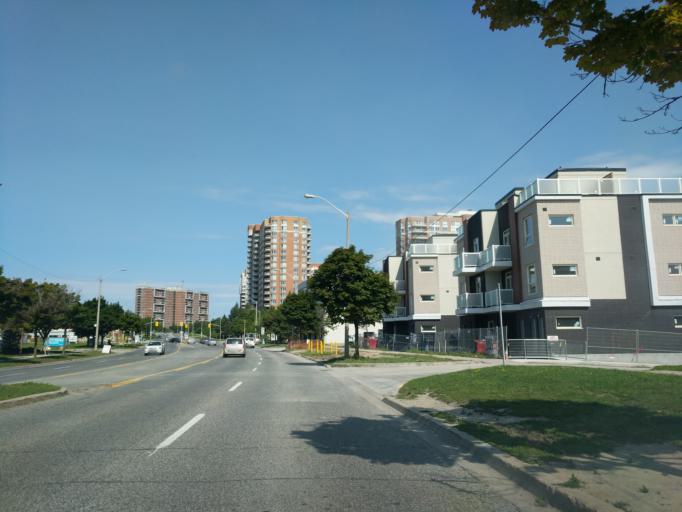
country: CA
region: Ontario
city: Scarborough
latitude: 43.8083
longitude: -79.2200
